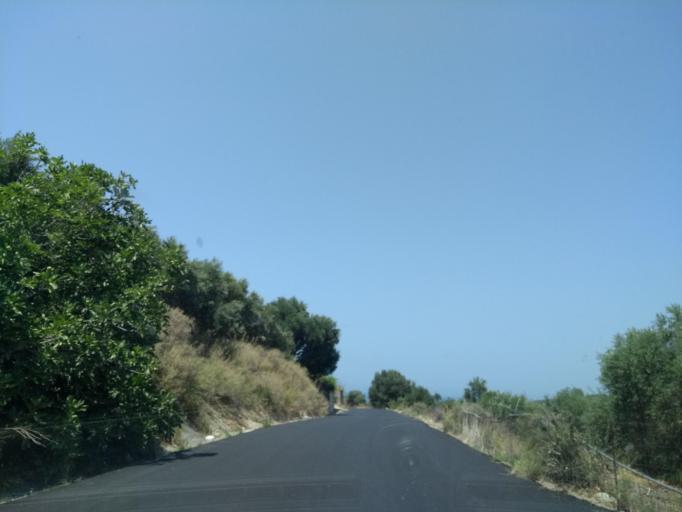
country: GR
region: Crete
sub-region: Nomos Chanias
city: Georgioupolis
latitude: 35.3302
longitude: 24.3009
